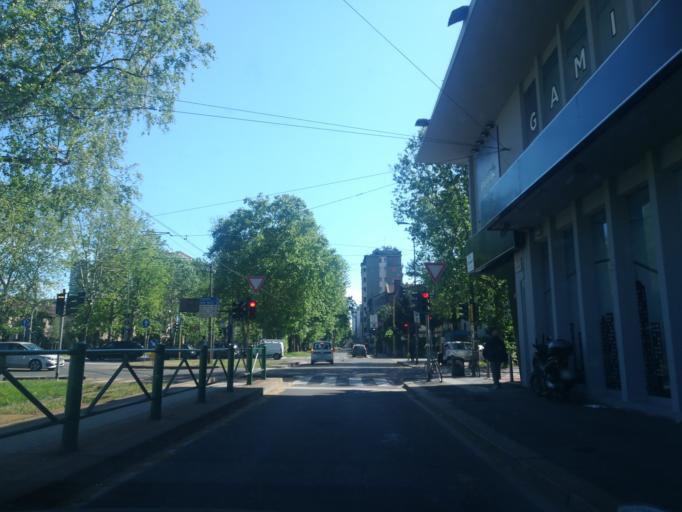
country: IT
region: Lombardy
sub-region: Citta metropolitana di Milano
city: Milano
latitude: 45.4960
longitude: 9.1943
